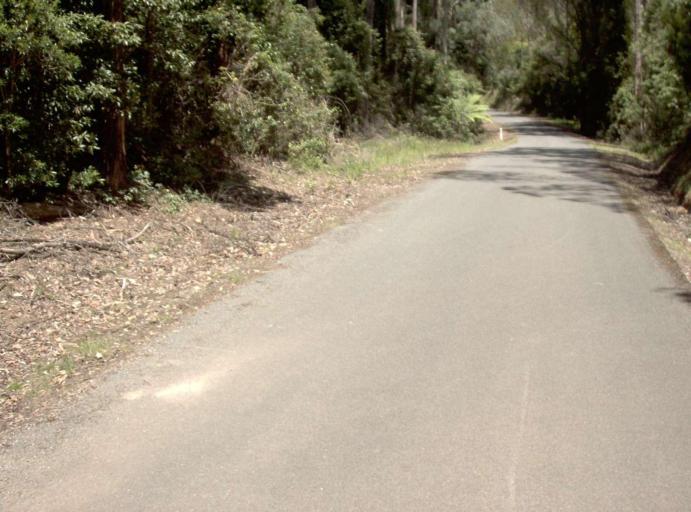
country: AU
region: New South Wales
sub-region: Bombala
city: Bombala
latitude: -37.4931
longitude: 148.9254
